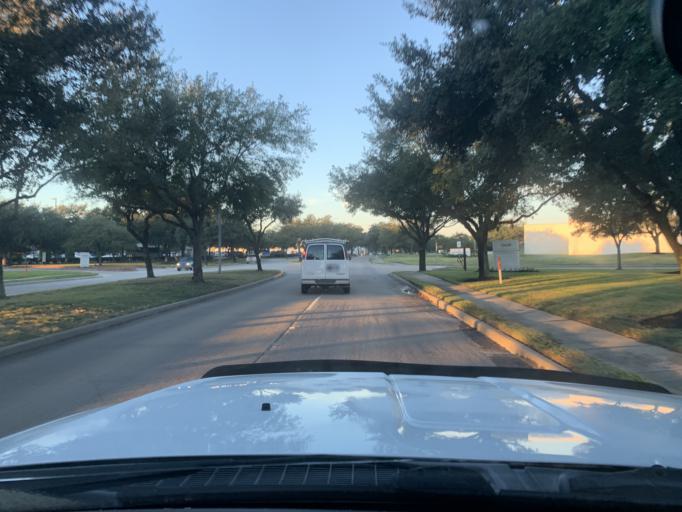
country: US
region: Texas
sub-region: Fort Bend County
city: Meadows Place
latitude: 29.6468
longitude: -95.6041
